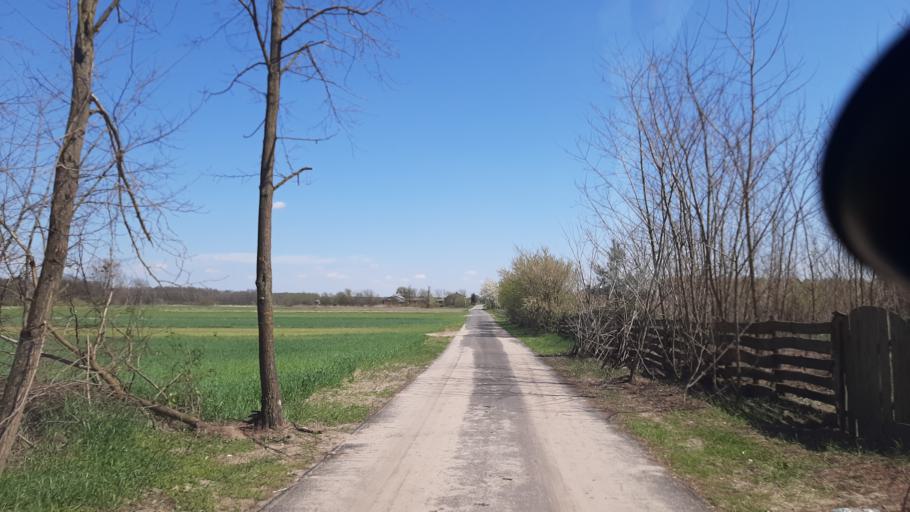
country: PL
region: Lublin Voivodeship
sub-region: Powiat lubelski
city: Garbow
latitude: 51.4030
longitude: 22.3189
